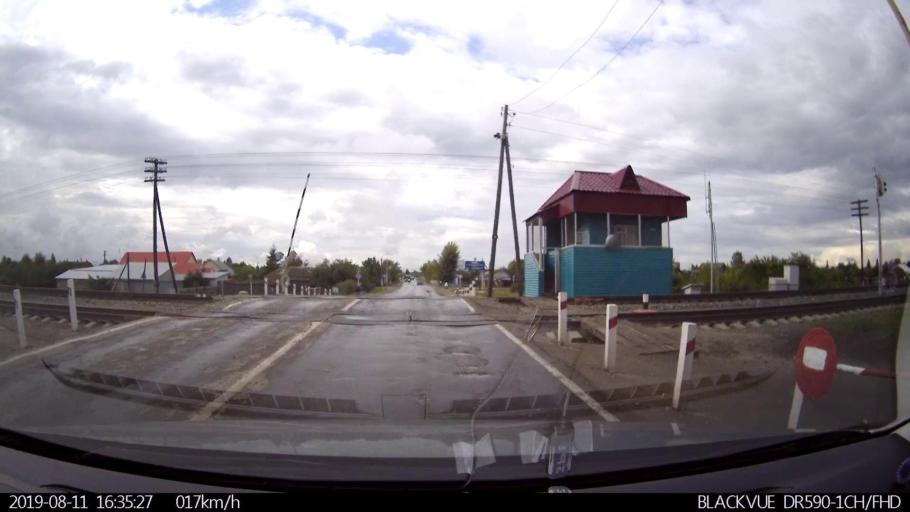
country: RU
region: Ulyanovsk
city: Mayna
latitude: 54.1150
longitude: 47.6153
